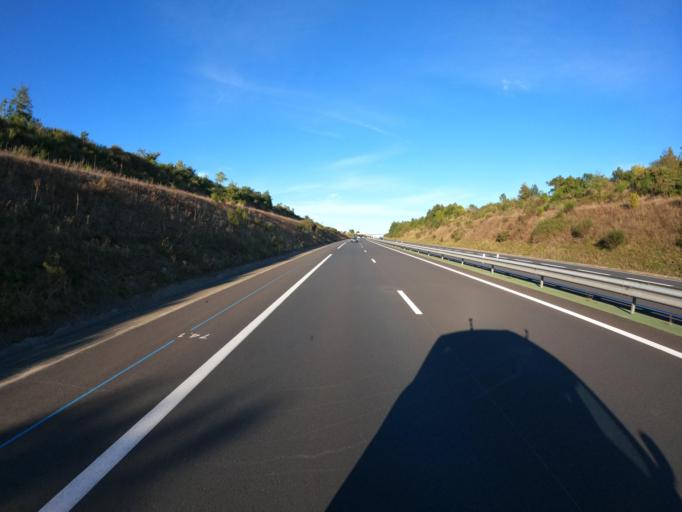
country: FR
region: Pays de la Loire
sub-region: Departement de la Vendee
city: La Gaubretiere
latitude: 46.9187
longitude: -1.0377
